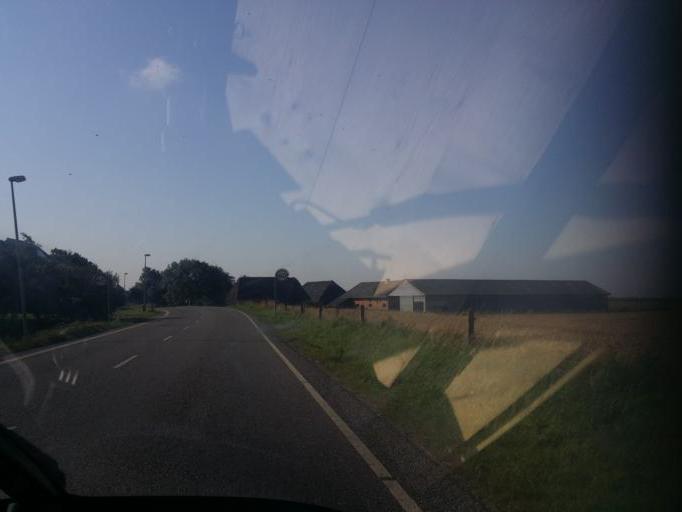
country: DE
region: Schleswig-Holstein
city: Neukirchen
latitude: 54.9057
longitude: 8.7490
